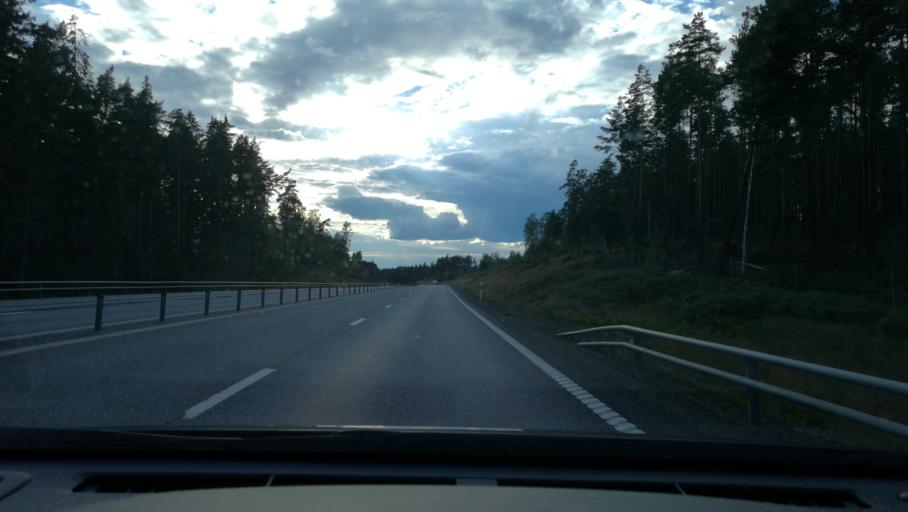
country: SE
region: OEstergoetland
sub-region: Norrkopings Kommun
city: Svartinge
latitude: 58.6648
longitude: 16.0207
